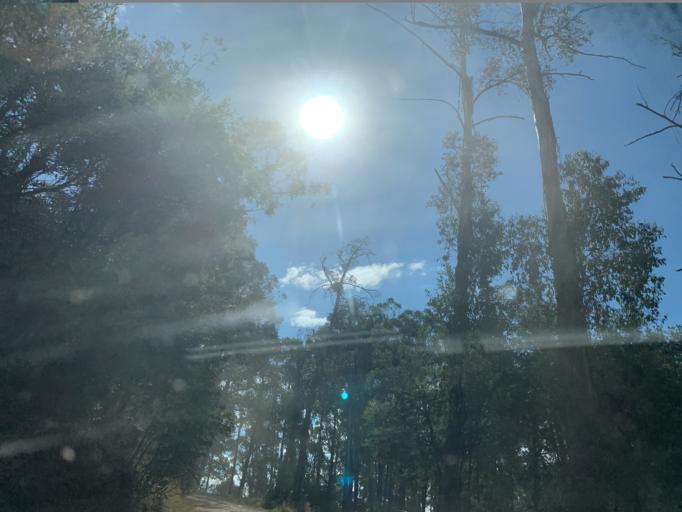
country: AU
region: Victoria
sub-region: Mansfield
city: Mansfield
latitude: -37.0970
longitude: 146.4983
